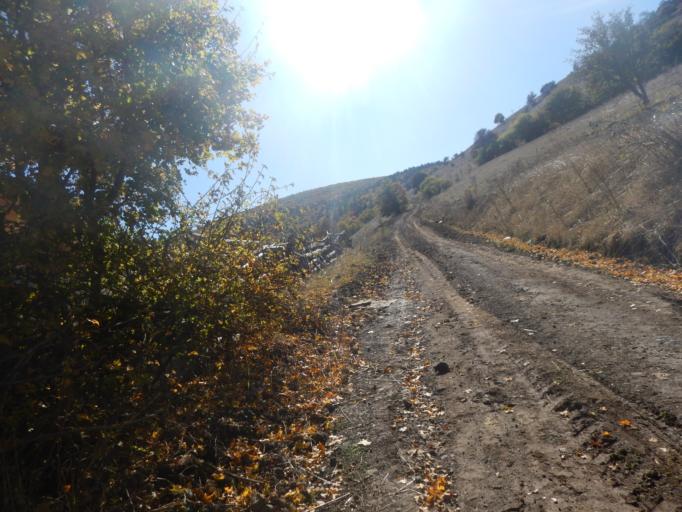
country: TR
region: Ordu
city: Mesudiye
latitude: 40.4327
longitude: 37.7711
